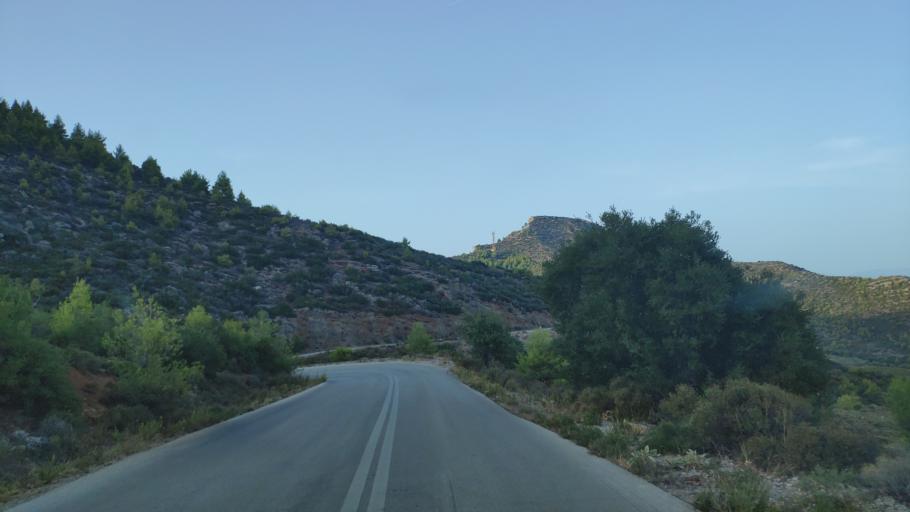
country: GR
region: West Greece
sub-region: Nomos Achaias
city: Aiyira
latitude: 38.0919
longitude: 22.4083
